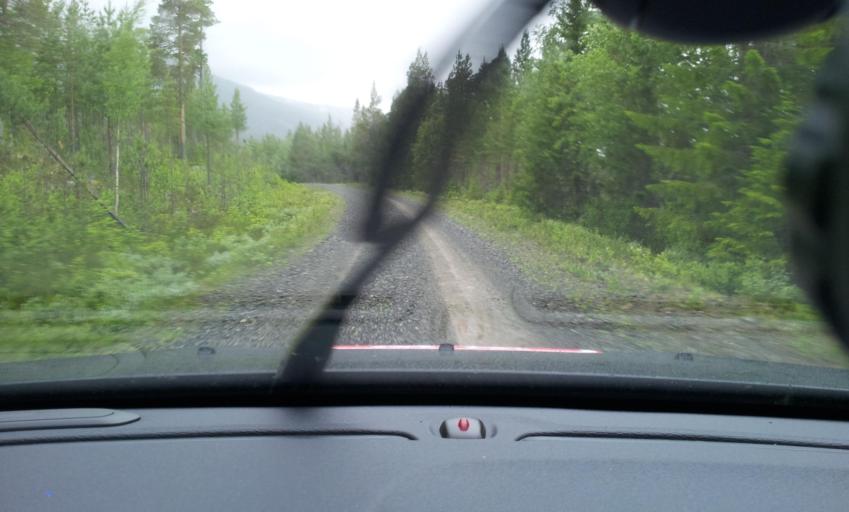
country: SE
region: Jaemtland
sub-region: Are Kommun
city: Jarpen
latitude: 63.1949
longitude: 13.3985
